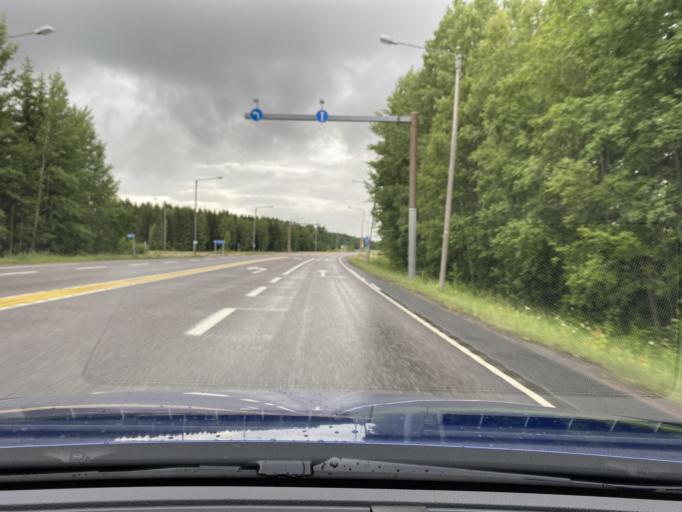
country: FI
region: Uusimaa
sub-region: Helsinki
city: Hyvinge
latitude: 60.5772
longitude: 24.7968
